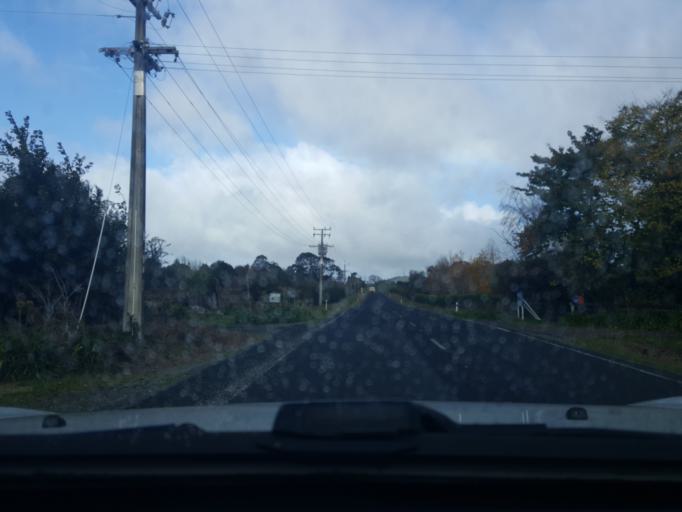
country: NZ
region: Auckland
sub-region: Auckland
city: Pukekohe East
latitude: -37.3067
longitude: 175.0116
